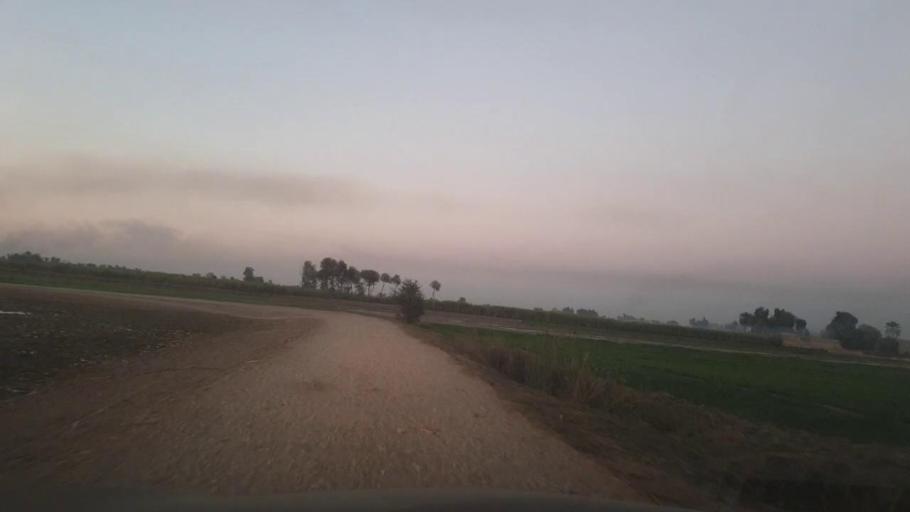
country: PK
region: Sindh
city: Ghotki
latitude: 28.0354
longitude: 69.3490
